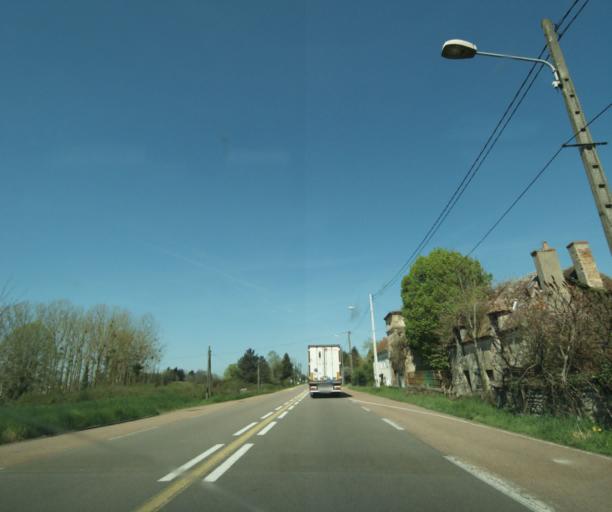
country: FR
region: Bourgogne
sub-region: Departement de la Nievre
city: Chantenay-Saint-Imbert
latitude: 46.7287
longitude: 3.1731
